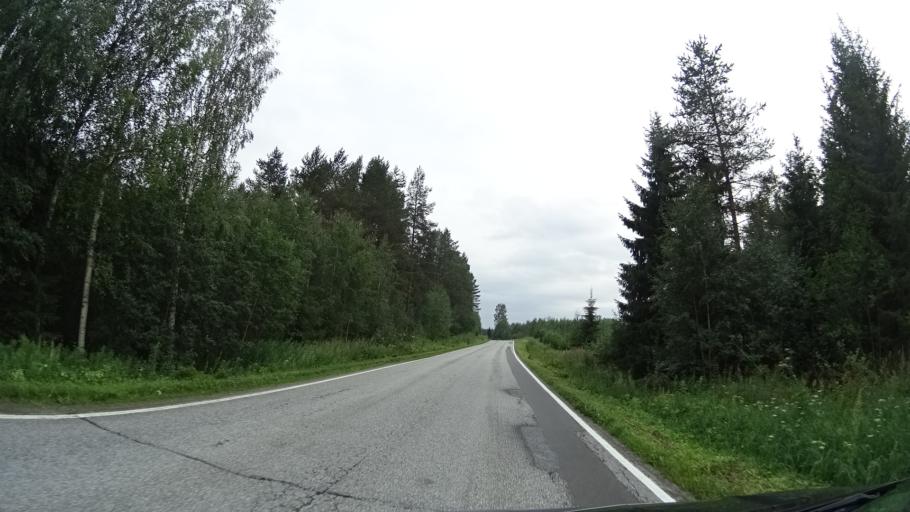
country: FI
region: Southern Savonia
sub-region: Savonlinna
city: Punkaharju
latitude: 61.7585
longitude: 29.5213
